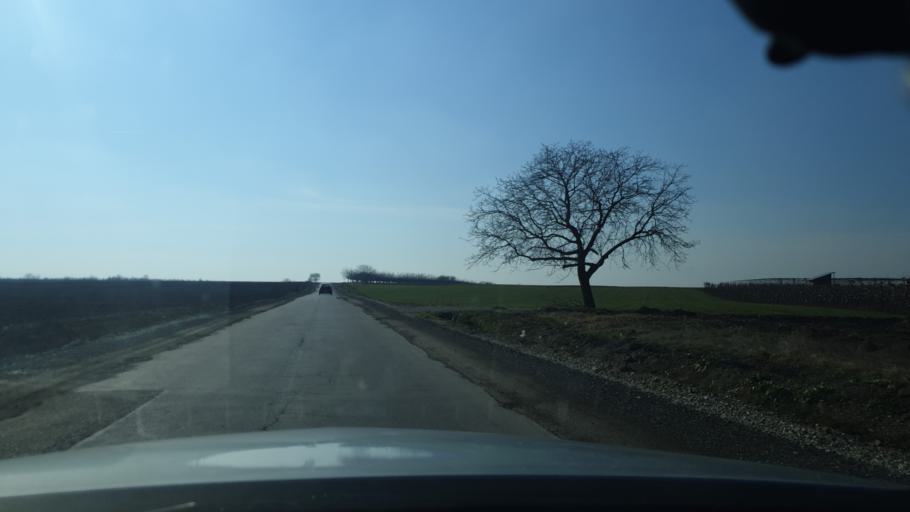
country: RS
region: Autonomna Pokrajina Vojvodina
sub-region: Sremski Okrug
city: Irig
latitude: 45.0837
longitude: 19.8498
